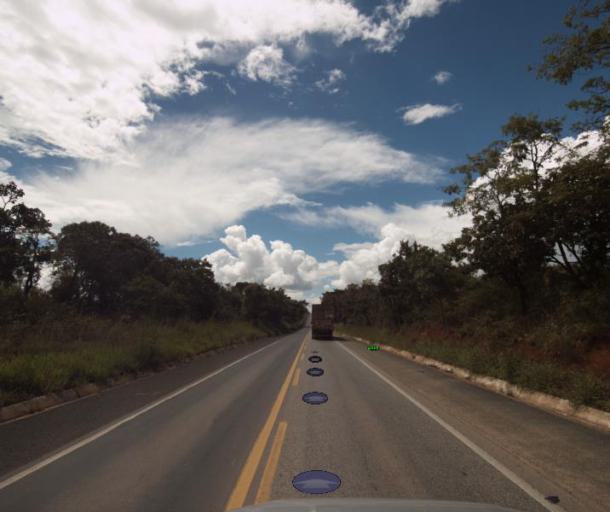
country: BR
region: Goias
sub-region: Uruacu
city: Uruacu
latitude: -14.1281
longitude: -49.1103
